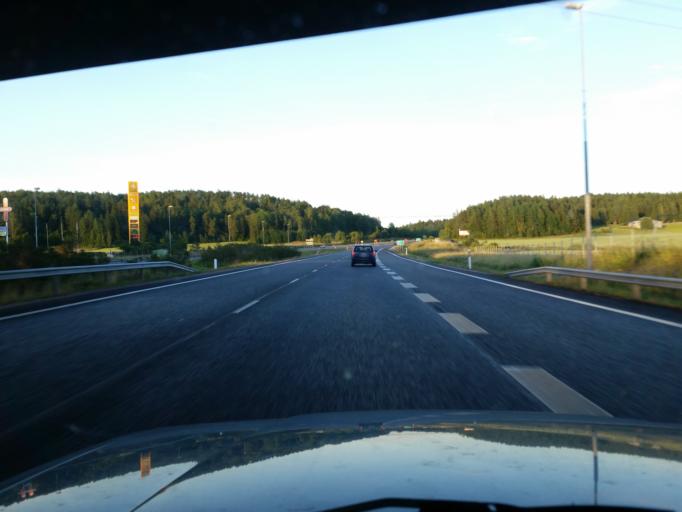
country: FI
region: Varsinais-Suomi
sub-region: Turku
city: Paimio
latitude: 60.4424
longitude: 22.6021
